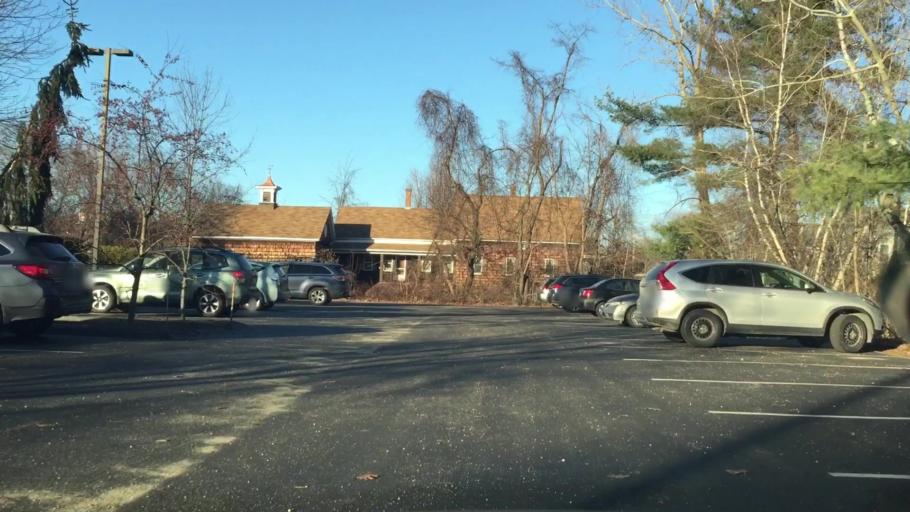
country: US
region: New Hampshire
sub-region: Cheshire County
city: Keene
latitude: 42.9318
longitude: -72.2926
